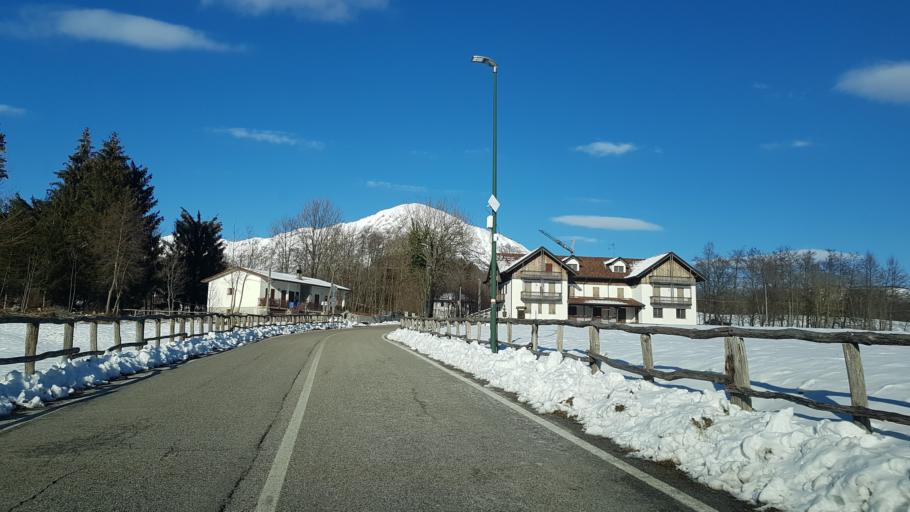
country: IT
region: Friuli Venezia Giulia
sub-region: Provincia di Udine
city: Forgaria nel Friuli
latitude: 46.2438
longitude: 12.9902
